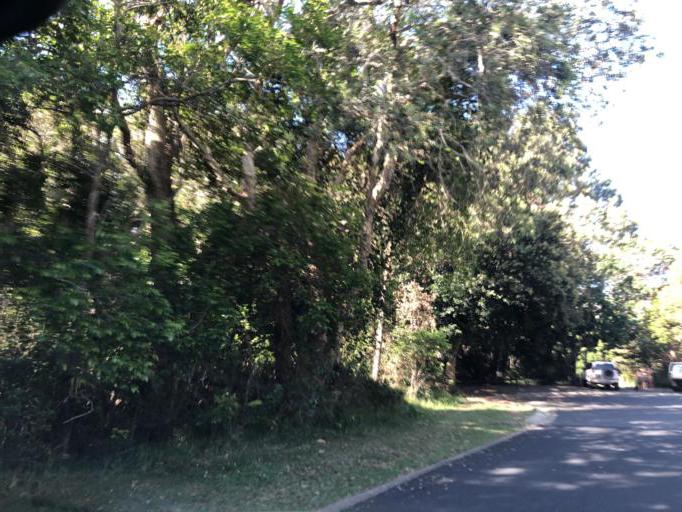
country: AU
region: New South Wales
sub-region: Coffs Harbour
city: Moonee Beach
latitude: -30.2312
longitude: 153.1524
